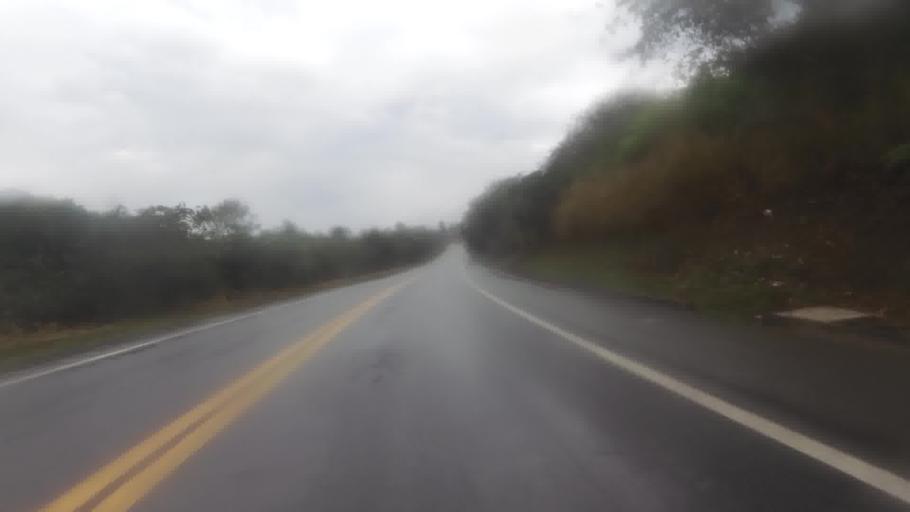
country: BR
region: Espirito Santo
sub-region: Cachoeiro De Itapemirim
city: Cachoeiro de Itapemirim
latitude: -21.0254
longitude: -41.1587
